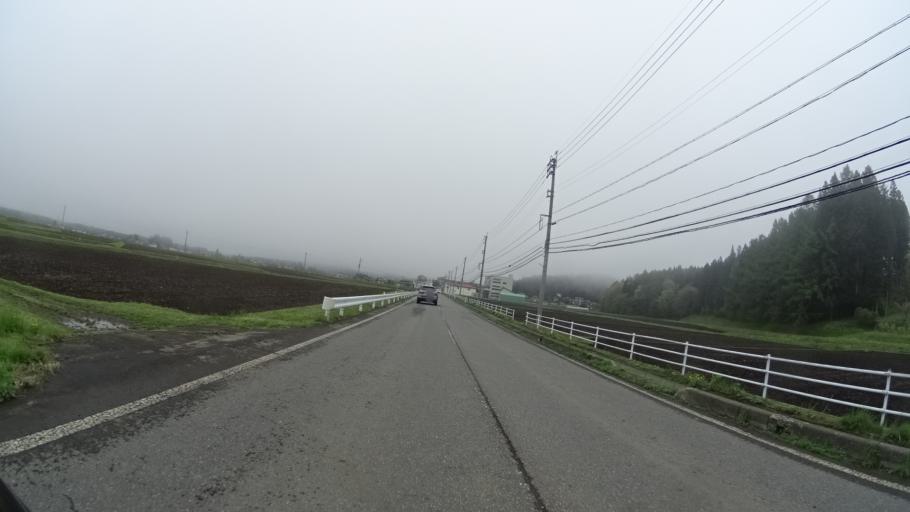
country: JP
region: Nagano
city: Nagano-shi
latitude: 36.7703
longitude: 138.2000
